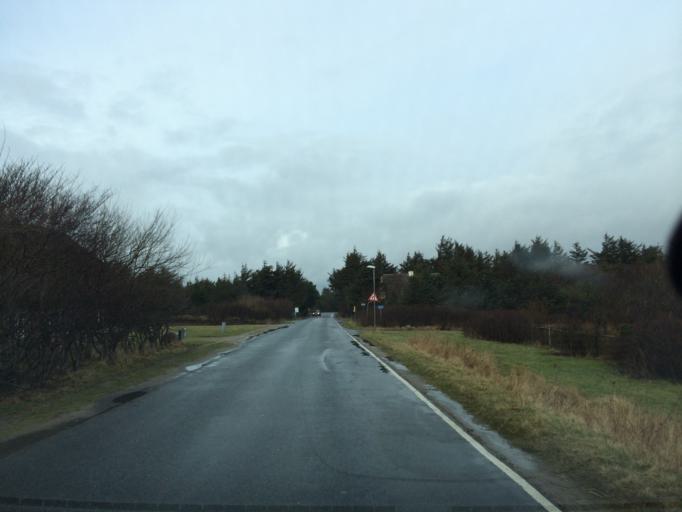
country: DK
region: Central Jutland
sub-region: Holstebro Kommune
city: Ulfborg
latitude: 56.2577
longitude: 8.1406
